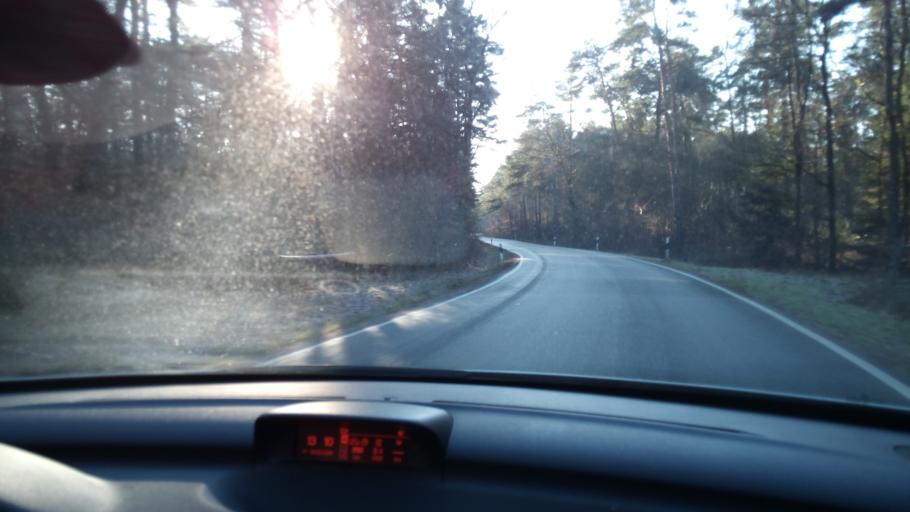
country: DE
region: Schleswig-Holstein
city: Gottin
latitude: 53.5209
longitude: 10.7040
